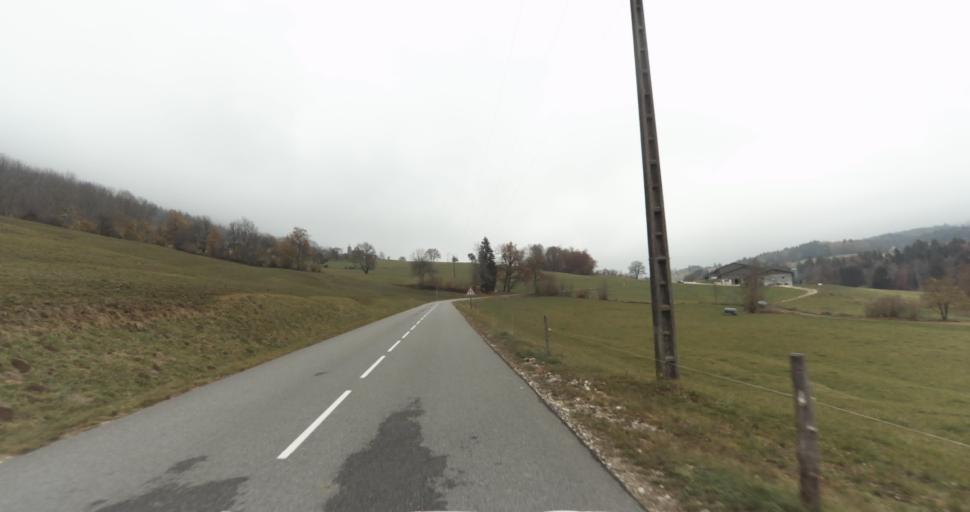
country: FR
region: Rhone-Alpes
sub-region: Departement de la Haute-Savoie
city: Gruffy
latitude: 45.7624
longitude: 6.1212
